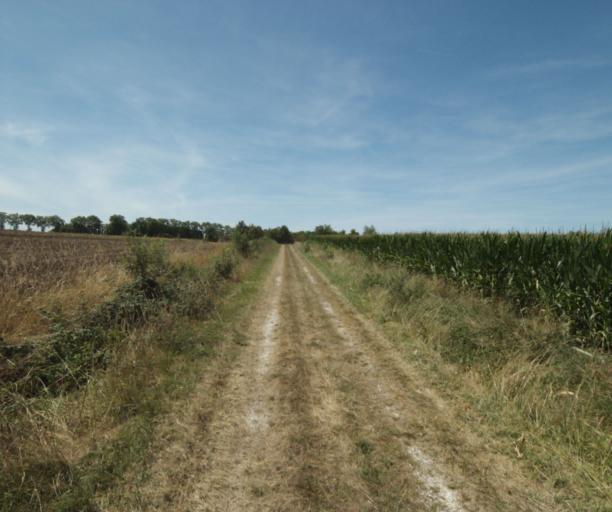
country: FR
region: Midi-Pyrenees
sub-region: Departement de la Haute-Garonne
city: Revel
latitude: 43.4994
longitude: 2.0169
